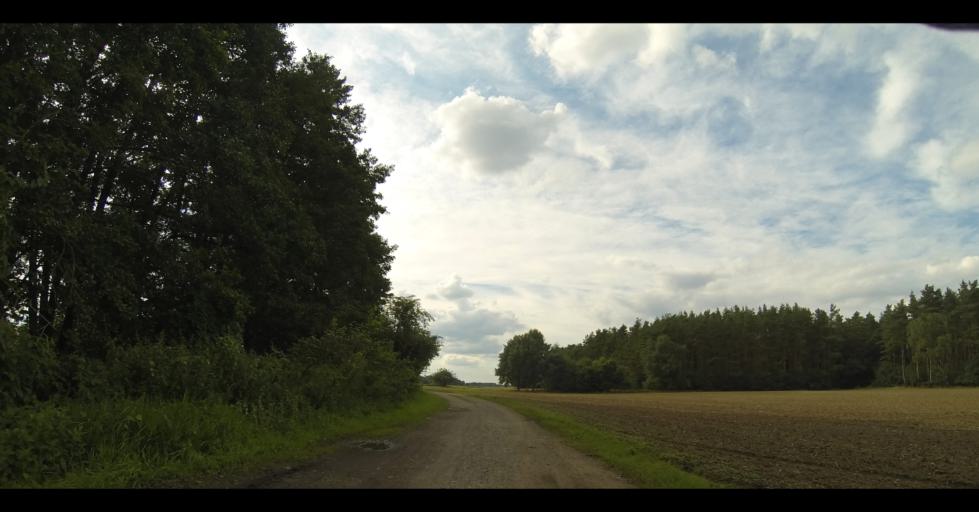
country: DE
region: Saxony
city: Radeburg
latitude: 51.2158
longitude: 13.7474
